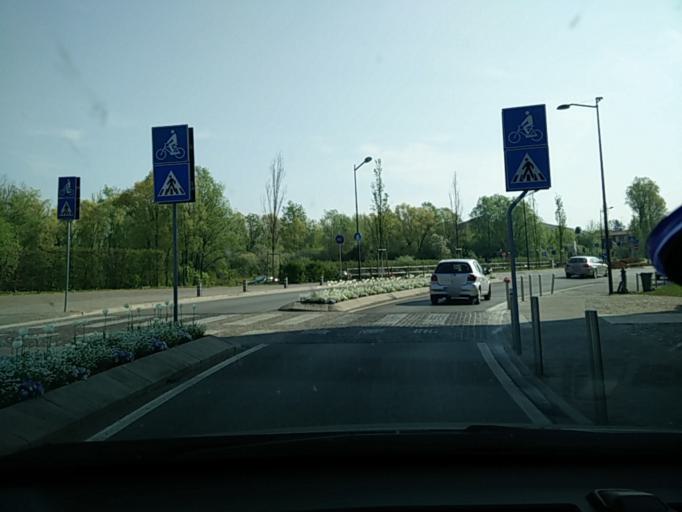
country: IT
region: Friuli Venezia Giulia
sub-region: Provincia di Pordenone
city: Pordenone
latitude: 45.9519
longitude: 12.6627
